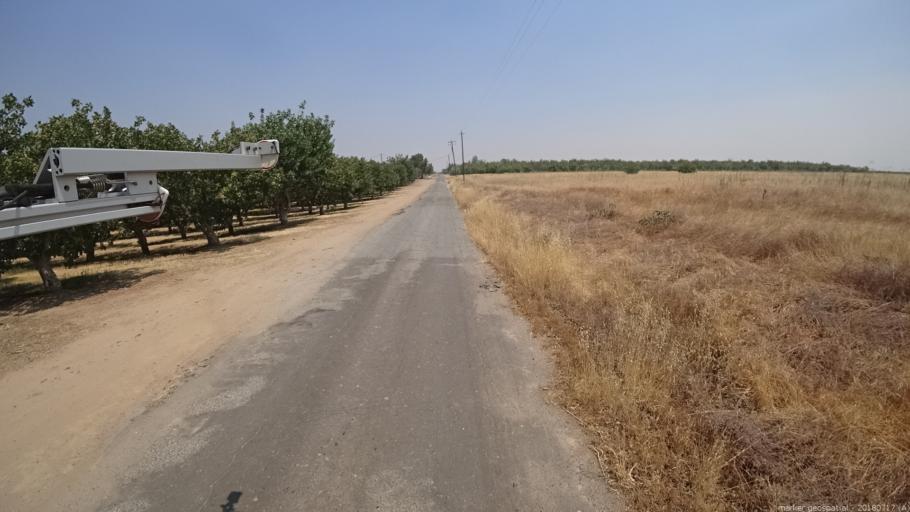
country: US
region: California
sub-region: Madera County
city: Fairmead
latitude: 37.1437
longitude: -120.1382
